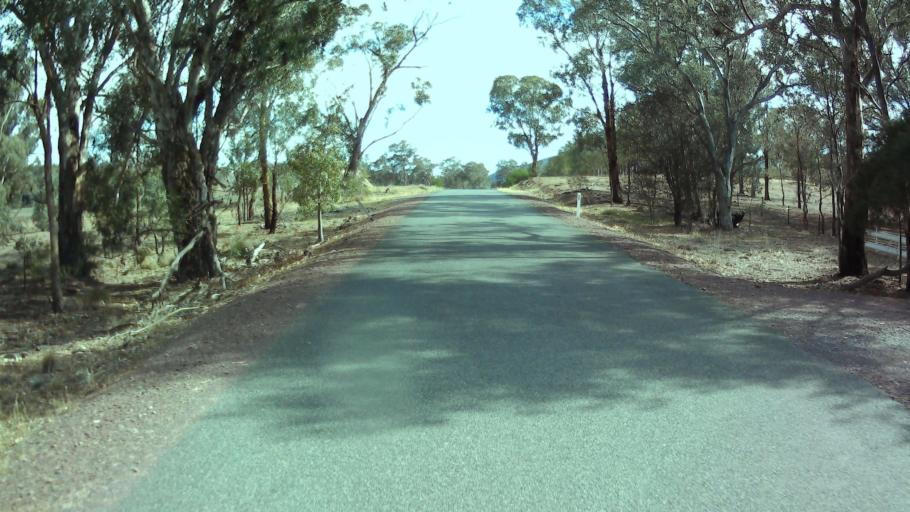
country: AU
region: New South Wales
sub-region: Weddin
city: Grenfell
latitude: -33.8148
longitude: 148.2919
